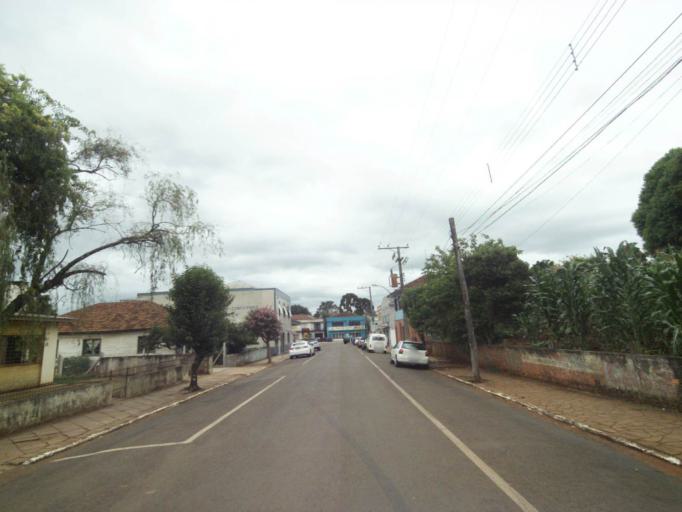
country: BR
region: Rio Grande do Sul
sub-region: Lagoa Vermelha
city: Lagoa Vermelha
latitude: -28.2110
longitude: -51.5304
